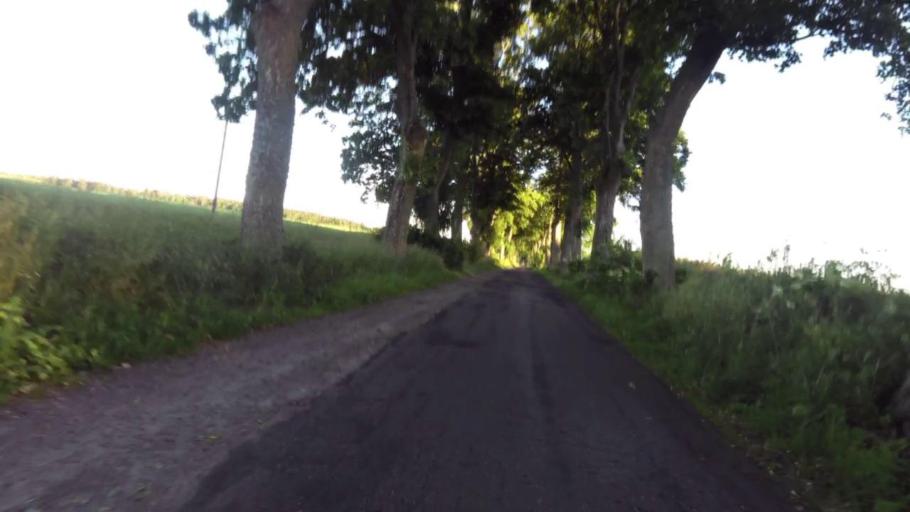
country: PL
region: West Pomeranian Voivodeship
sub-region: Koszalin
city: Koszalin
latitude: 54.0710
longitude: 16.1254
